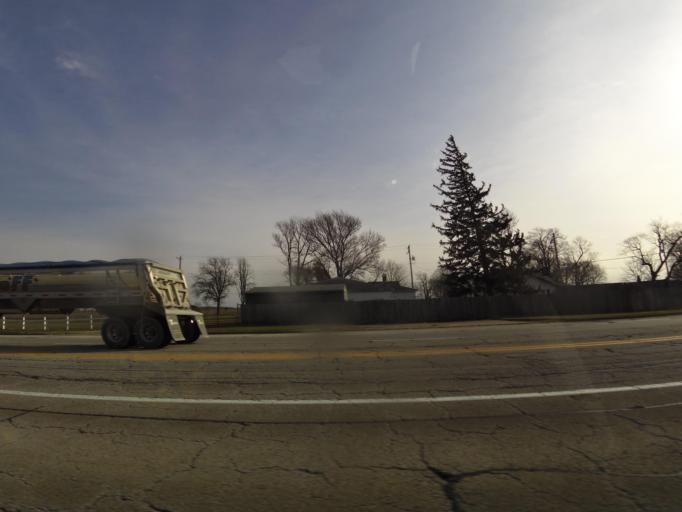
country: US
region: Illinois
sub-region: Macon County
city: Decatur
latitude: 39.7788
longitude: -88.9794
